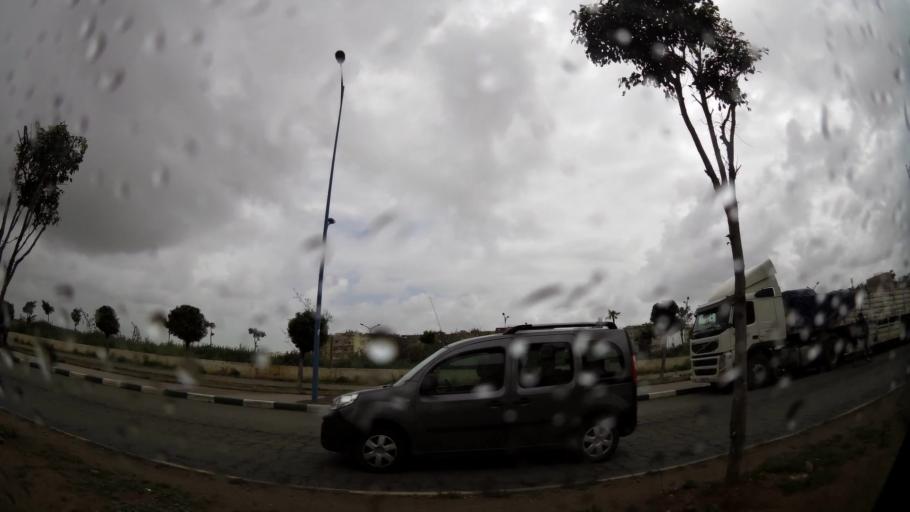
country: MA
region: Grand Casablanca
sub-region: Mediouna
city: Tit Mellil
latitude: 33.6171
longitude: -7.5002
